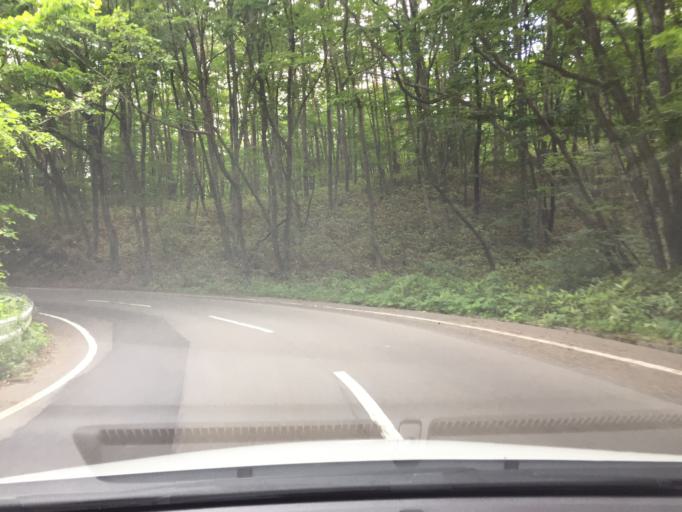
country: JP
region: Tochigi
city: Kuroiso
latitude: 37.2528
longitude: 140.0719
